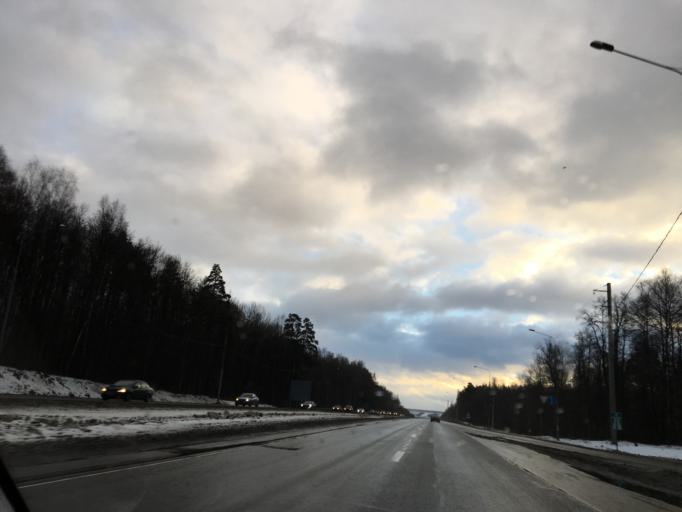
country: RU
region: Moskovskaya
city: Danki
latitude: 54.9039
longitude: 37.5116
